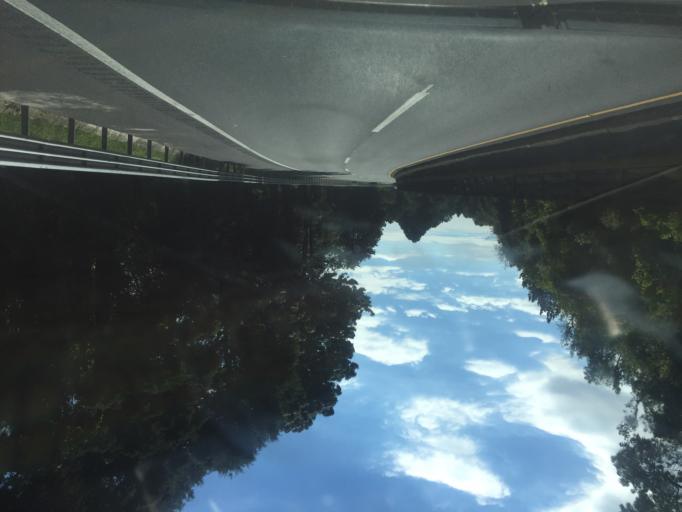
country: MX
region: Morelos
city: Tres Marias
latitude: 19.0362
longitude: -99.2277
